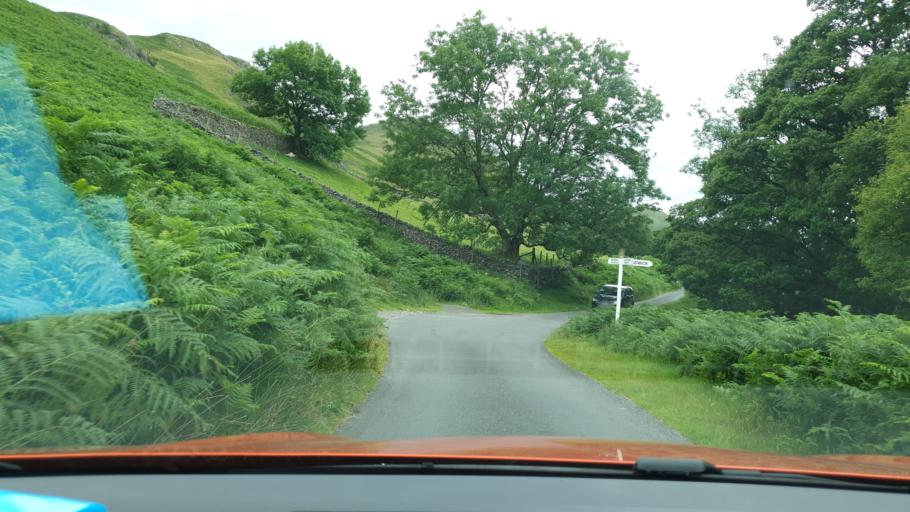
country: GB
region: England
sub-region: Cumbria
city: Ambleside
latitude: 54.5613
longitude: -2.8852
